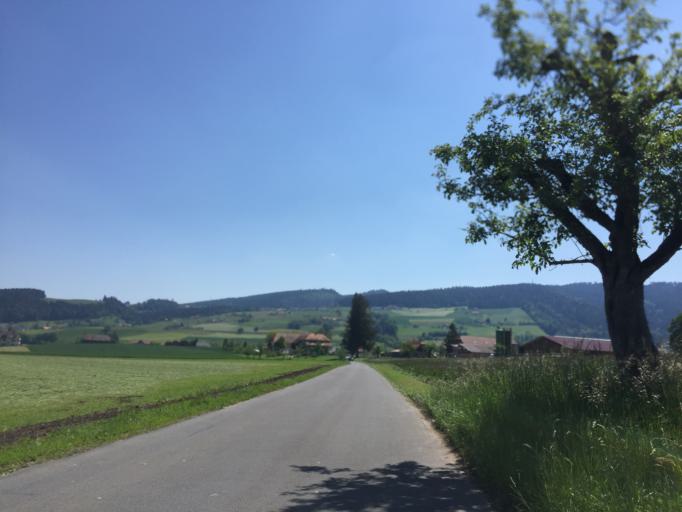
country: CH
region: Bern
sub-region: Bern-Mittelland District
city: Konolfingen
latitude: 46.8722
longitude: 7.6134
